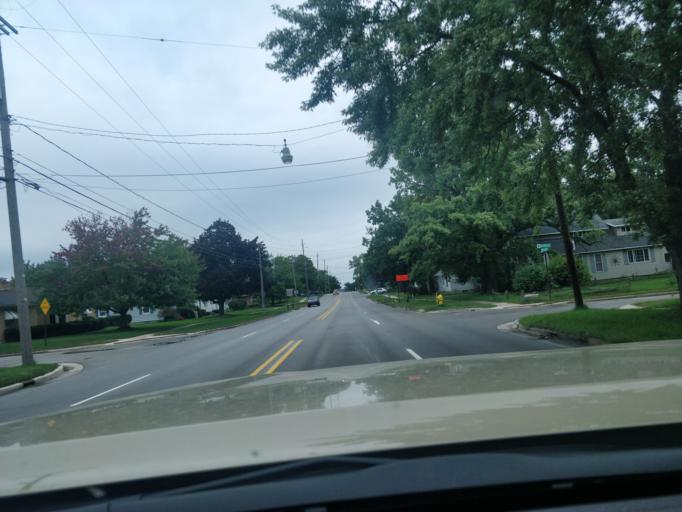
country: US
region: Michigan
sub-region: Kent County
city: Wyoming
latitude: 42.9151
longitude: -85.7249
